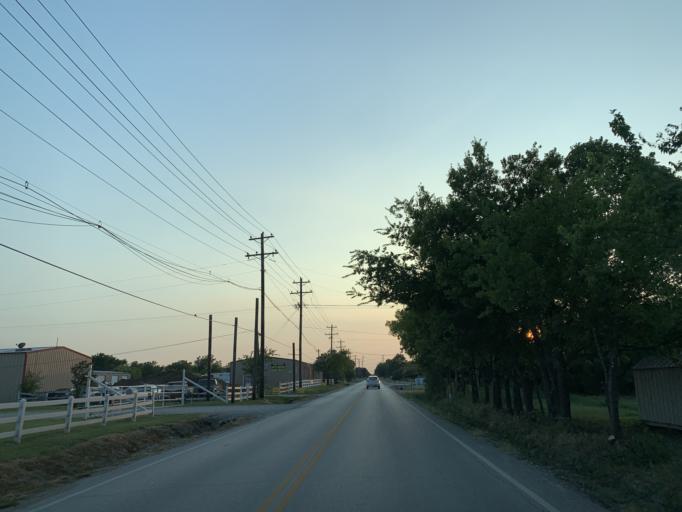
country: US
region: Texas
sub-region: Tarrant County
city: Keller
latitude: 32.9636
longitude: -97.2546
